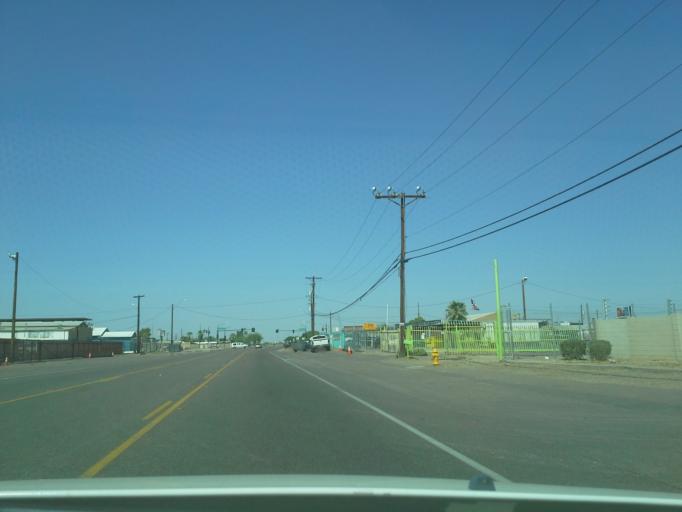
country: US
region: Arizona
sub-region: Maricopa County
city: Laveen
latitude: 33.4067
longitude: -112.1311
